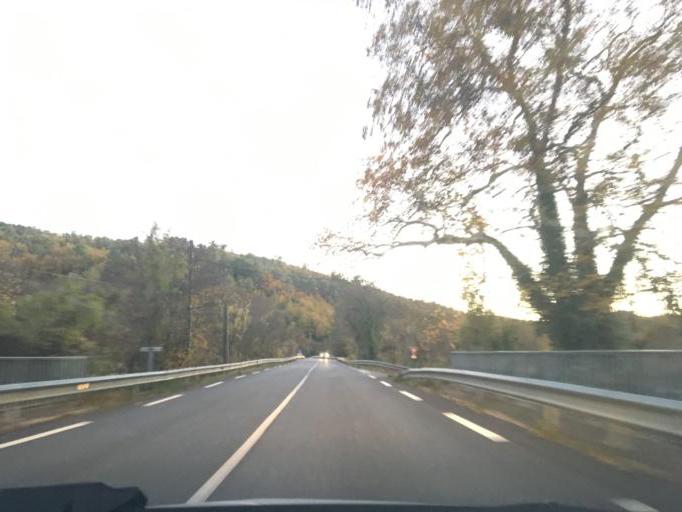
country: FR
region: Provence-Alpes-Cote d'Azur
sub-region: Departement du Var
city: Montferrat
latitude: 43.6043
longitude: 6.4787
